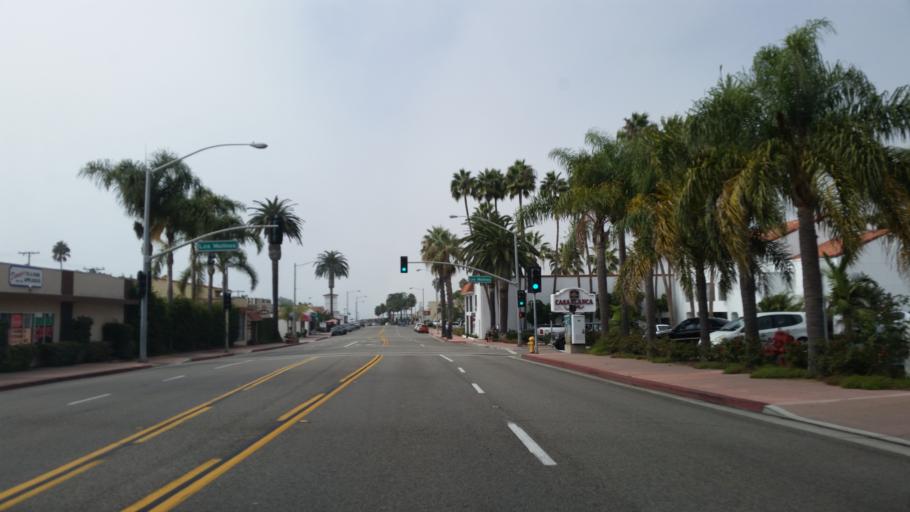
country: US
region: California
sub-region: Orange County
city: San Clemente
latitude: 33.4323
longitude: -117.6271
